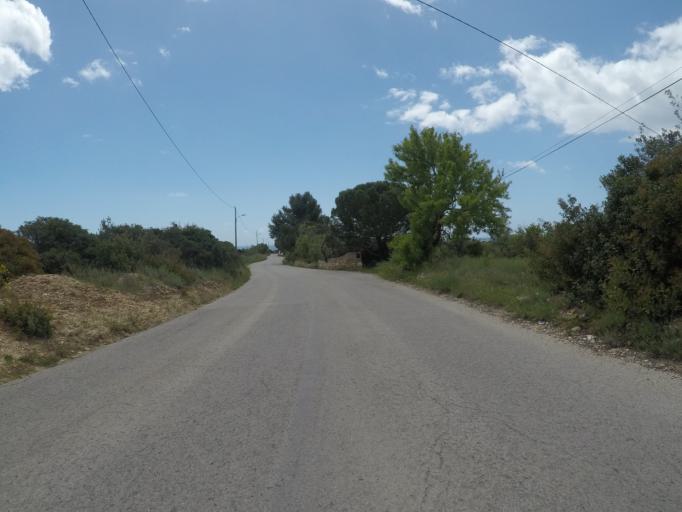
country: PT
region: Faro
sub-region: Lagoa
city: Carvoeiro
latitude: 37.0953
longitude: -8.4197
